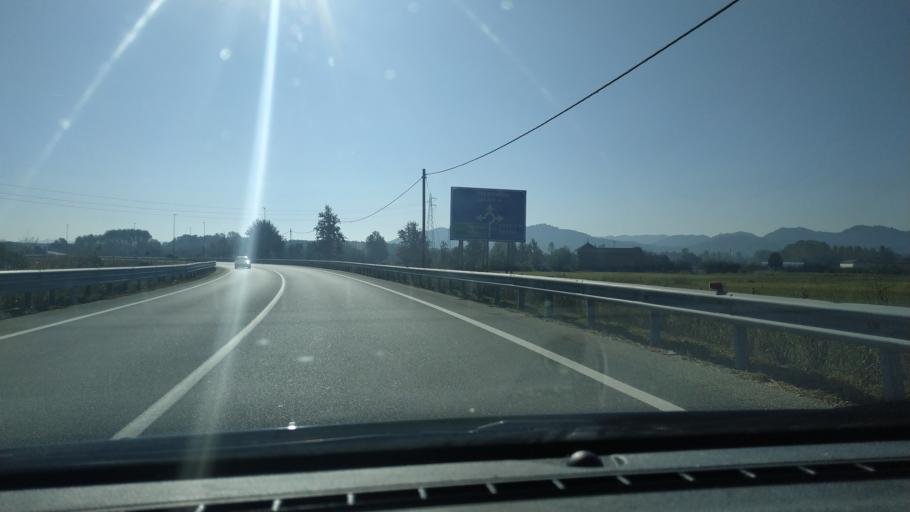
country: IT
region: Piedmont
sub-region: Provincia di Torino
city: Verolengo
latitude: 45.1872
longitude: 7.9557
